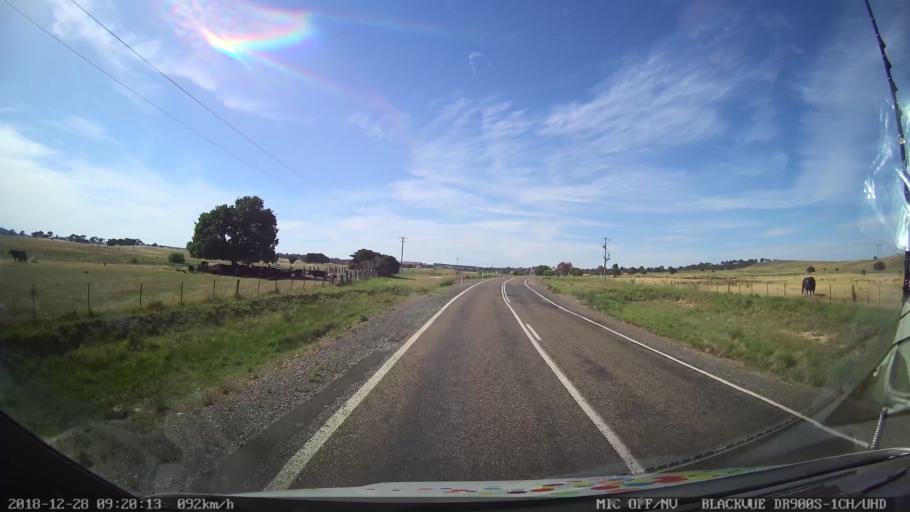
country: AU
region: New South Wales
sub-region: Upper Lachlan Shire
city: Crookwell
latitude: -34.3471
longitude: 149.3719
